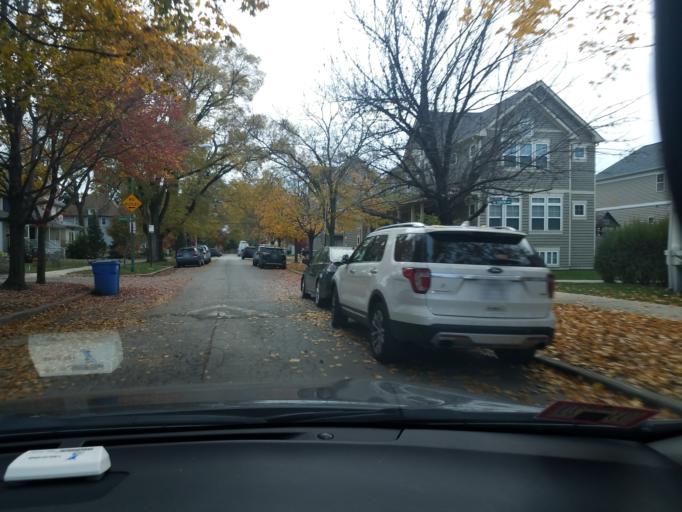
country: US
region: Illinois
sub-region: Cook County
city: Lincolnwood
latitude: 41.9524
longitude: -87.7410
